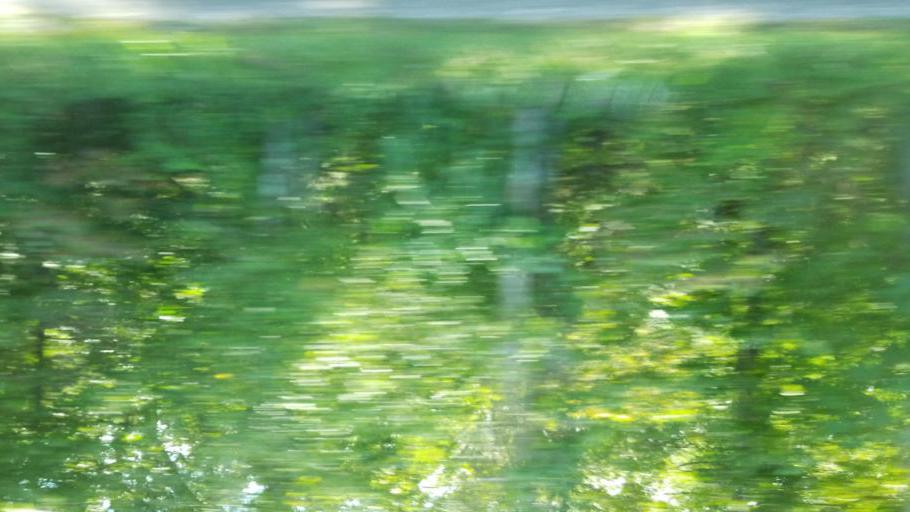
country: US
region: Illinois
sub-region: Williamson County
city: Johnston City
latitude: 37.7902
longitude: -88.8304
